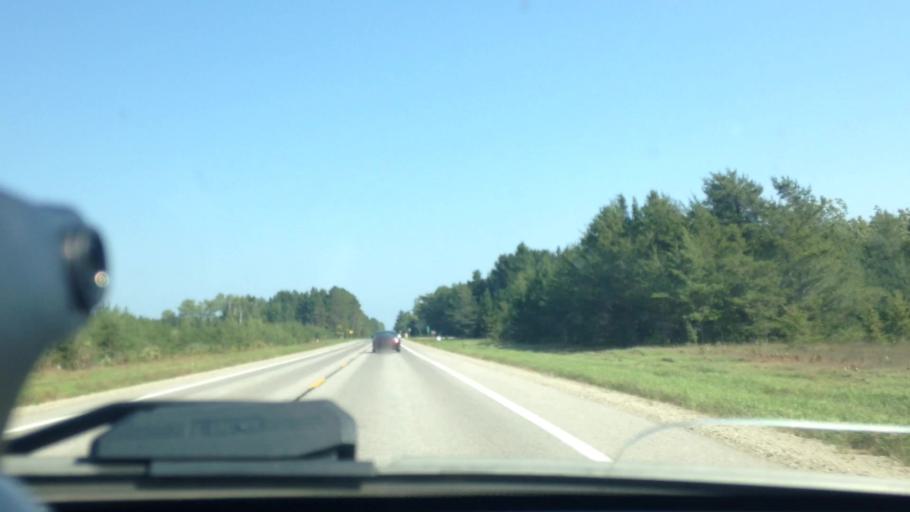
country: US
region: Michigan
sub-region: Luce County
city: Newberry
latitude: 46.3036
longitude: -85.4522
